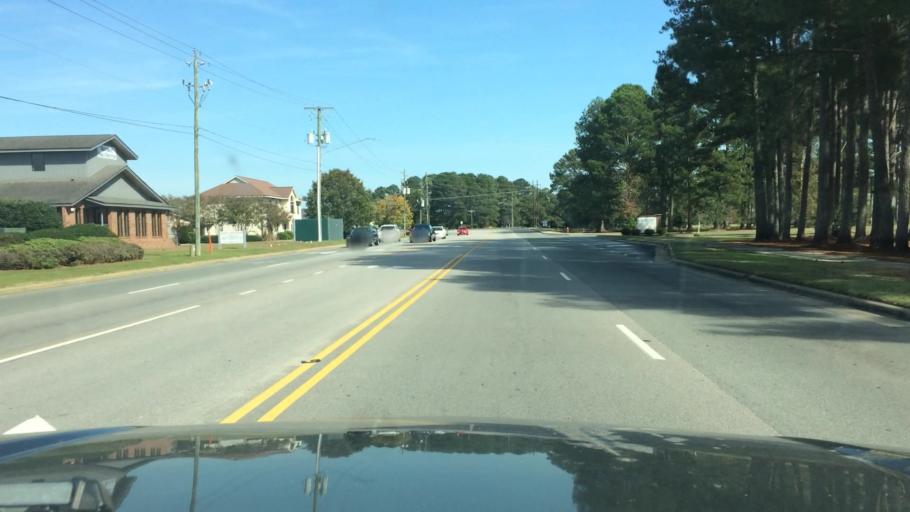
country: US
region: North Carolina
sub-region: Wayne County
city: Goldsboro
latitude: 35.4009
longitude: -77.9531
